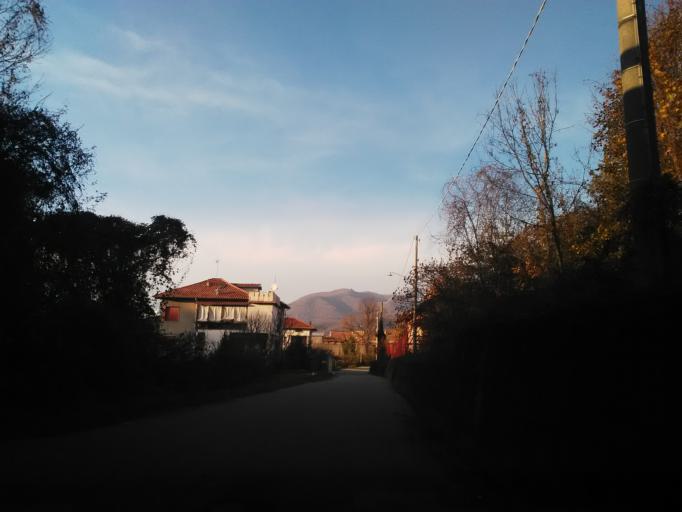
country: IT
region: Piedmont
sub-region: Provincia di Novara
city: Grignasco
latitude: 45.6715
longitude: 8.3444
